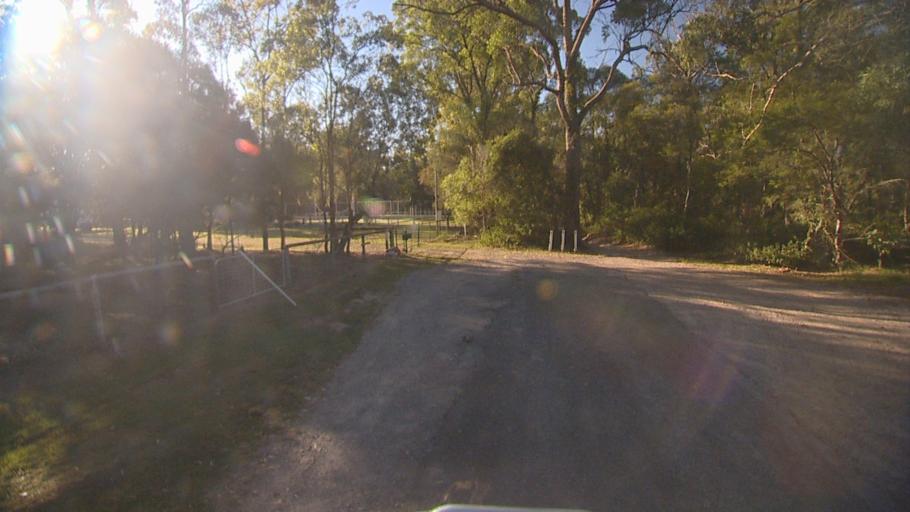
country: AU
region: Queensland
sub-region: Gold Coast
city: Yatala
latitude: -27.6624
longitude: 153.2455
